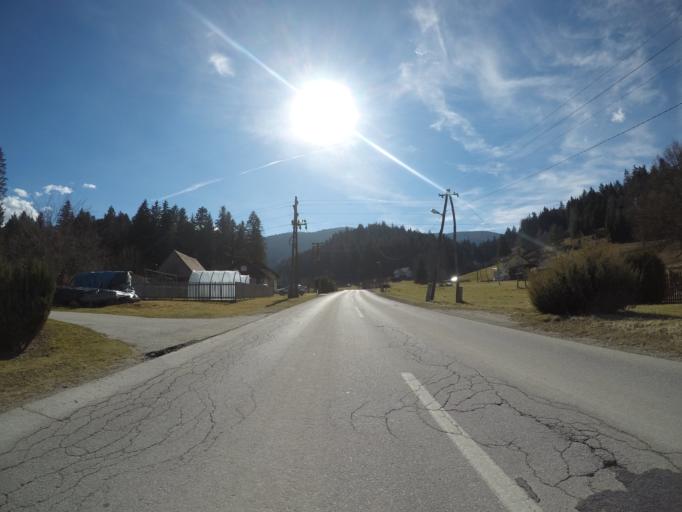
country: SI
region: Lovrenc na Pohorju
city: Lovrenc na Pohorju
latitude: 46.5433
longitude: 15.4232
